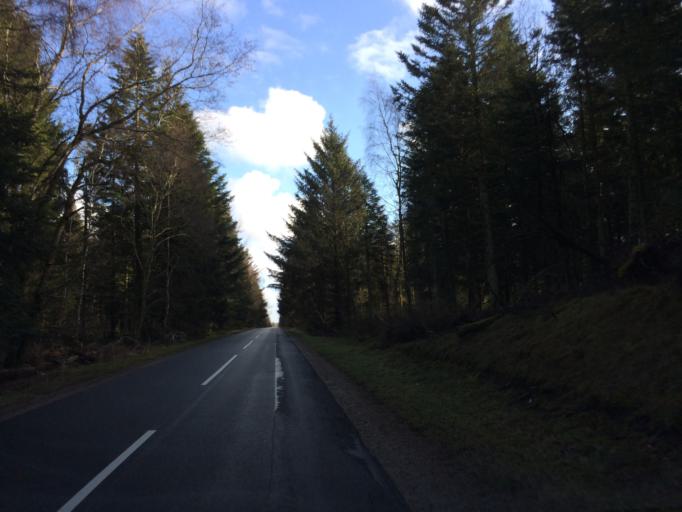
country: DK
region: Central Jutland
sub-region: Holstebro Kommune
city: Ulfborg
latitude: 56.2554
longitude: 8.3583
